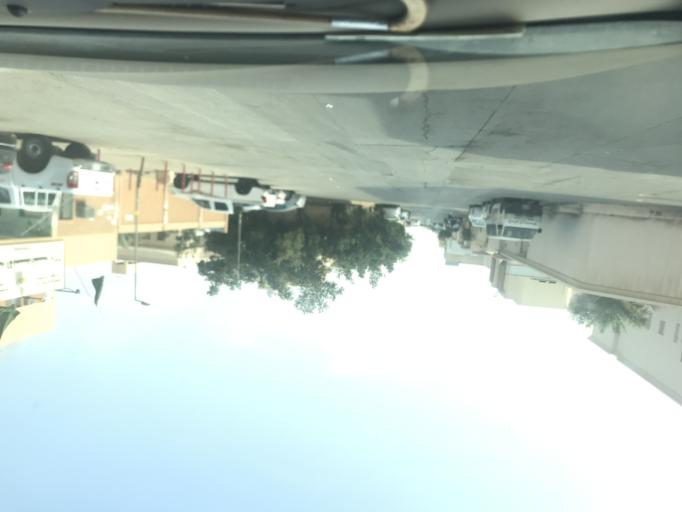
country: SA
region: Ar Riyad
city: Riyadh
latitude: 24.7305
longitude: 46.7674
